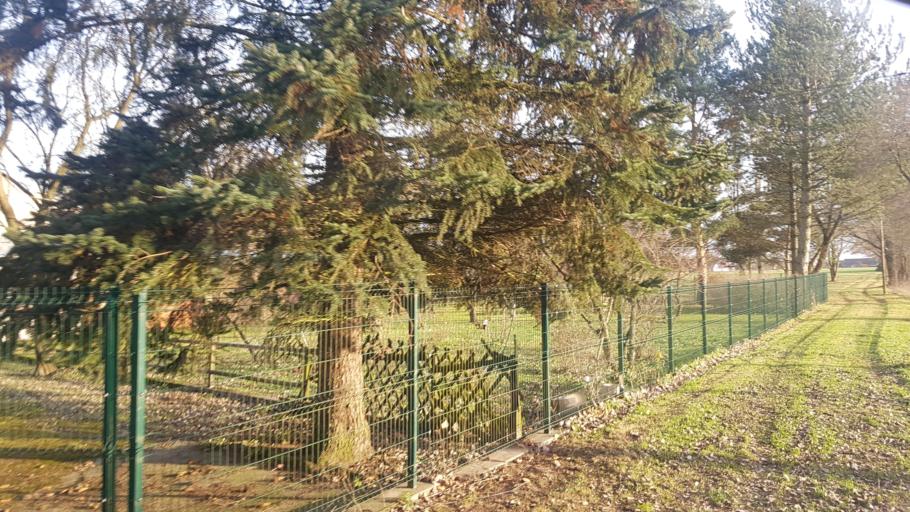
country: DE
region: Brandenburg
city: Doberlug-Kirchhain
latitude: 51.6591
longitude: 13.5175
